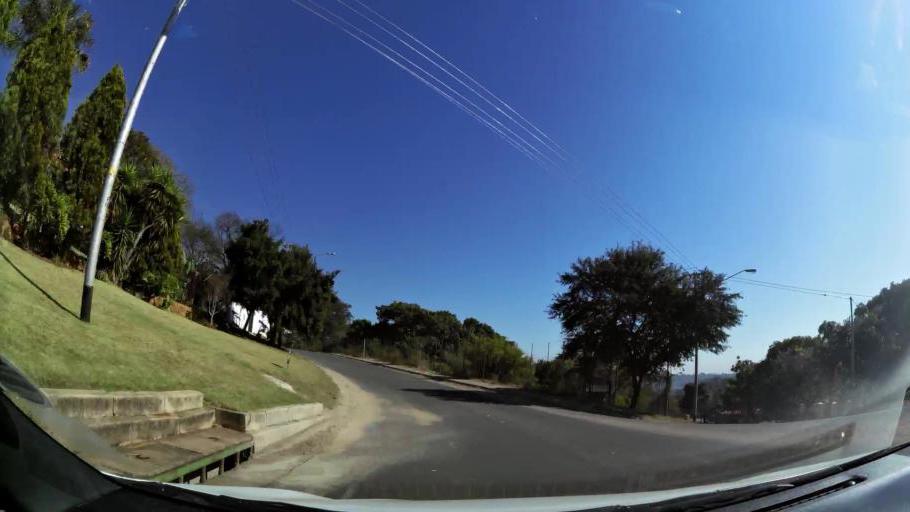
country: ZA
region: Gauteng
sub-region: City of Tshwane Metropolitan Municipality
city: Pretoria
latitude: -25.7795
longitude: 28.2213
